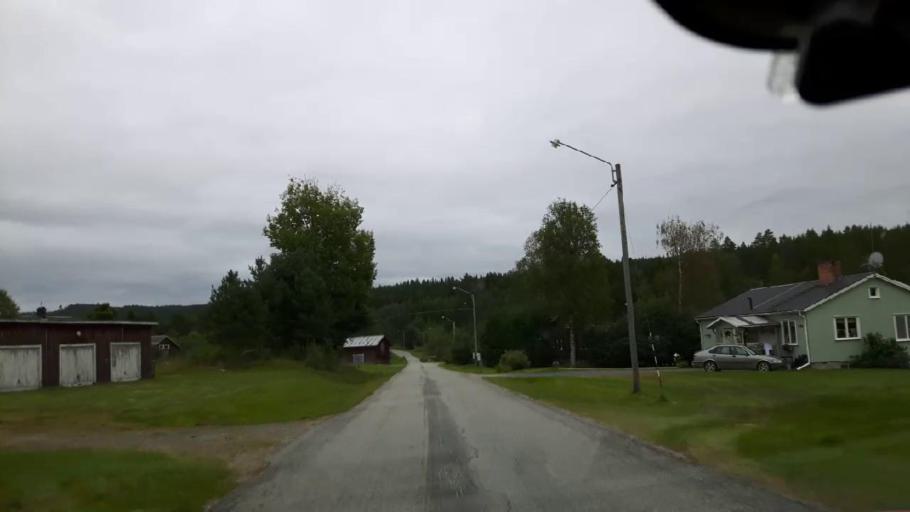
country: SE
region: Vaesternorrland
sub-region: Ange Kommun
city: Fransta
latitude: 62.7751
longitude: 15.9883
